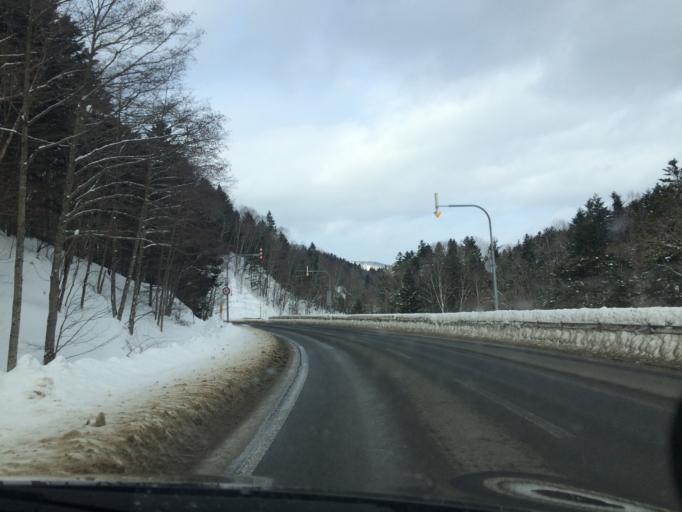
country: JP
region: Hokkaido
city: Shimo-furano
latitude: 42.9401
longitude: 142.3739
